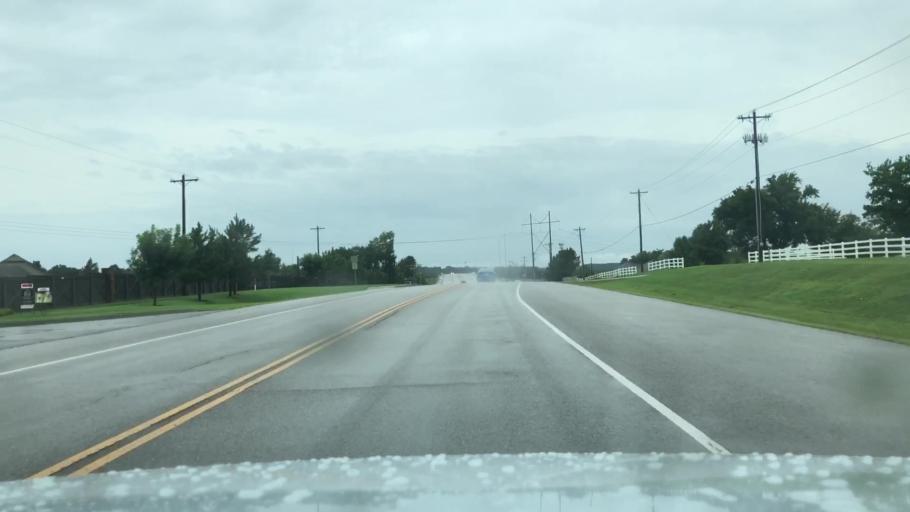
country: US
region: Oklahoma
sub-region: Tulsa County
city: Jenks
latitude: 36.0029
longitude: -96.0041
